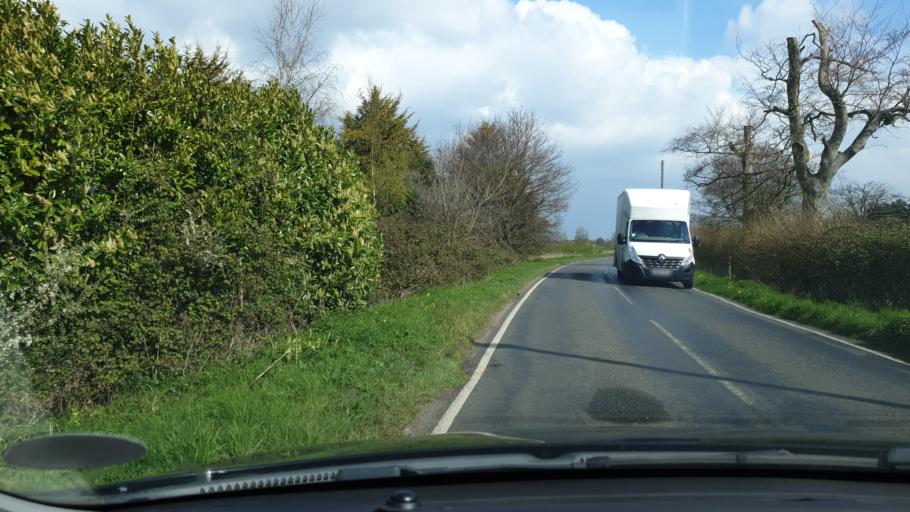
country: GB
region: England
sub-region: Essex
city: Great Bentley
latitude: 51.8676
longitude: 1.1013
